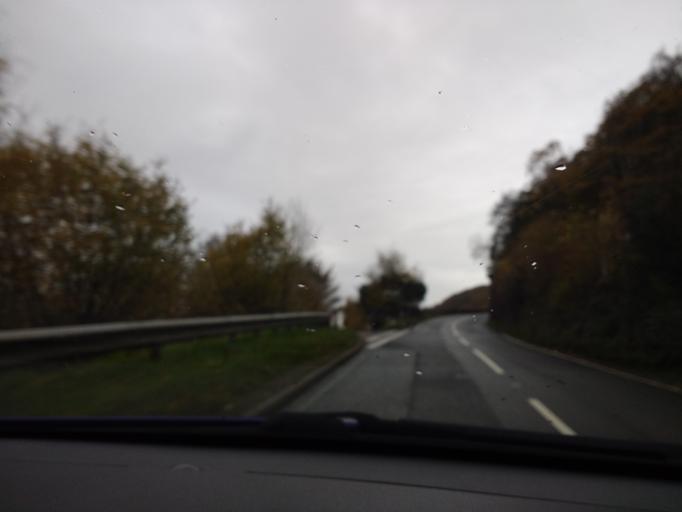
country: GB
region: England
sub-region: Cumbria
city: Millom
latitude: 54.2766
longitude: -3.2371
